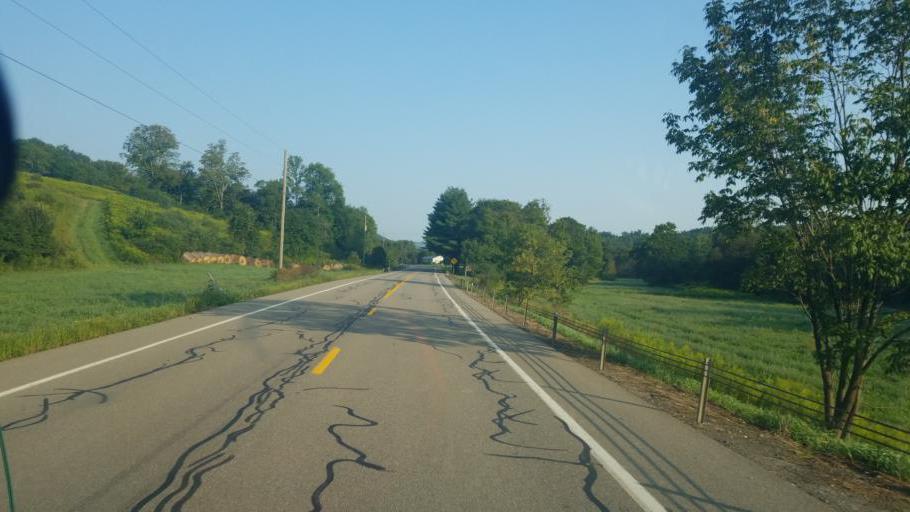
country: US
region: Pennsylvania
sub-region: Tioga County
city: Westfield
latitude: 42.0053
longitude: -77.5099
